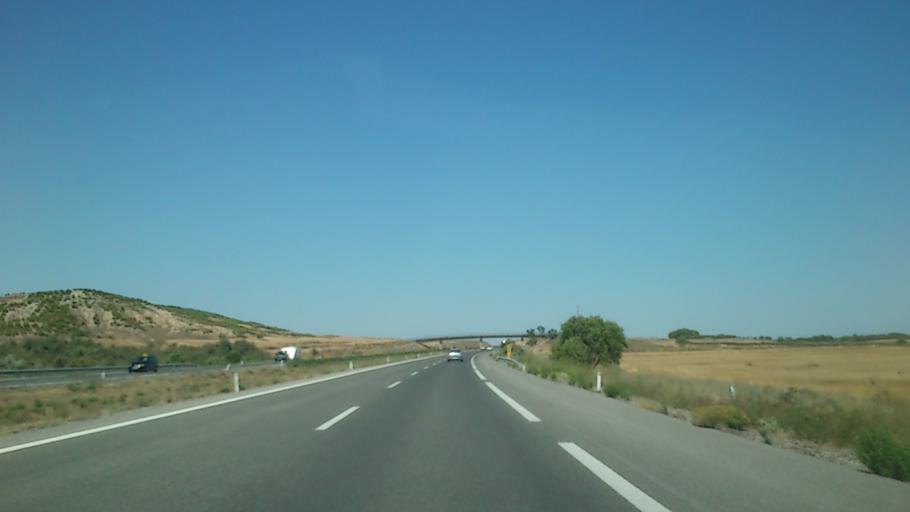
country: ES
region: Aragon
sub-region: Provincia de Zaragoza
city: Frescano
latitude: 41.9276
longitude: -1.4931
